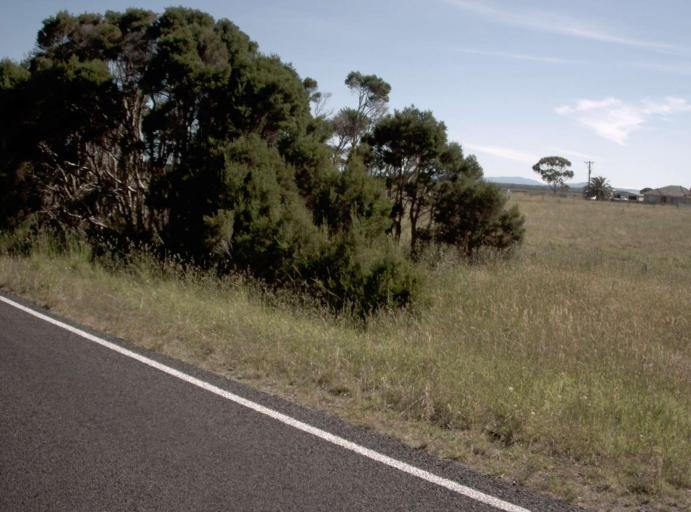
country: AU
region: Victoria
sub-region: Latrobe
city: Traralgon
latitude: -38.6238
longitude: 146.6734
